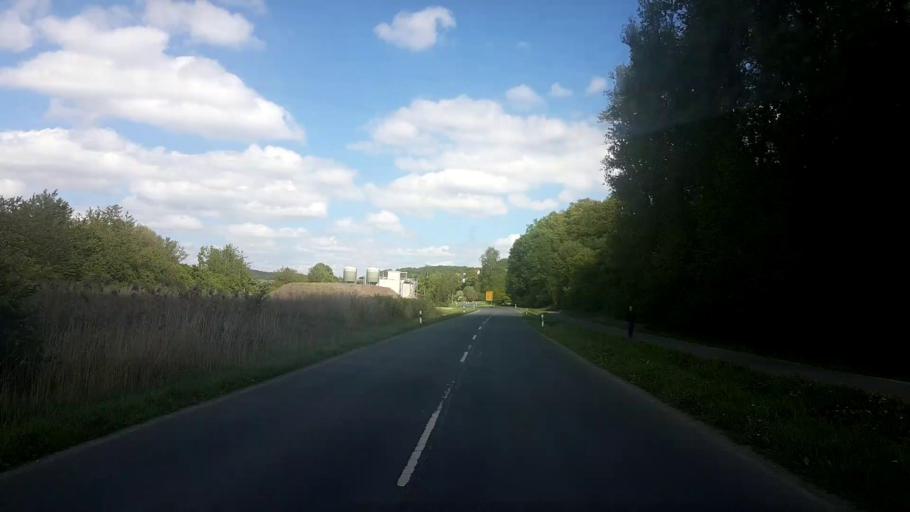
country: DE
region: Bavaria
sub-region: Upper Franconia
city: Niederfullbach
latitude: 50.2092
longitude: 10.9786
